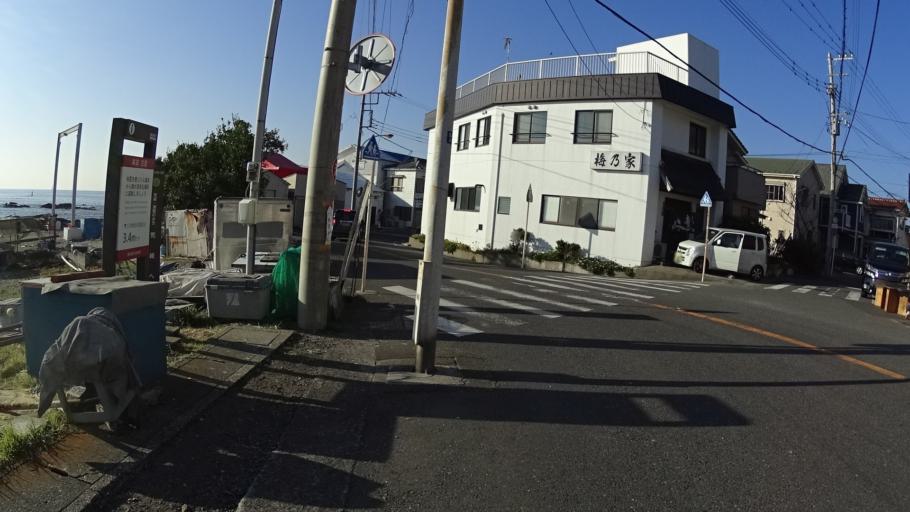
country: JP
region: Kanagawa
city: Miura
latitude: 35.2008
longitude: 139.6062
